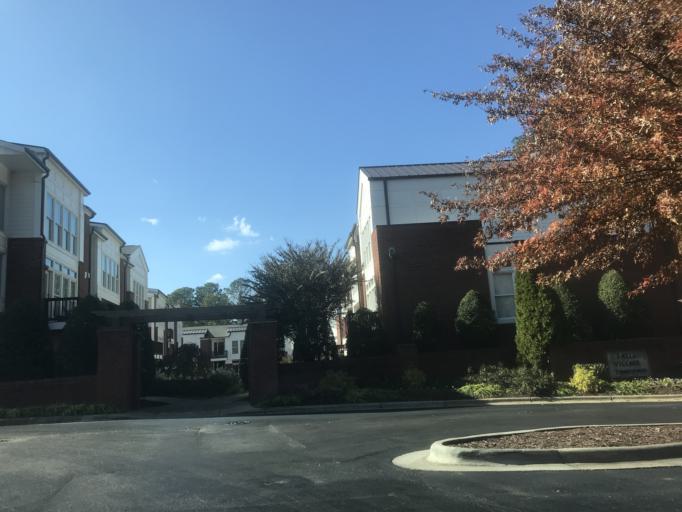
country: US
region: North Carolina
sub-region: Wake County
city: West Raleigh
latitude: 35.8751
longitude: -78.6256
